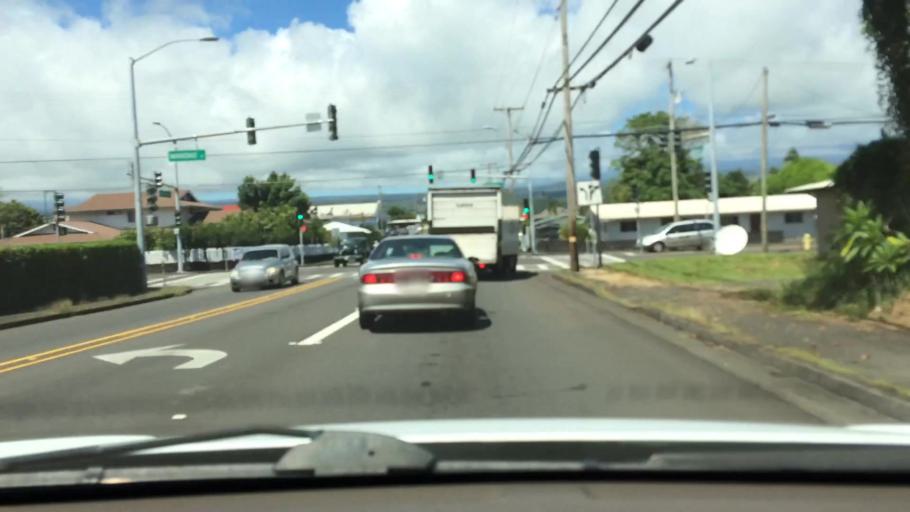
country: US
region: Hawaii
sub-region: Hawaii County
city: Hilo
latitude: 19.7118
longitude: -155.0697
